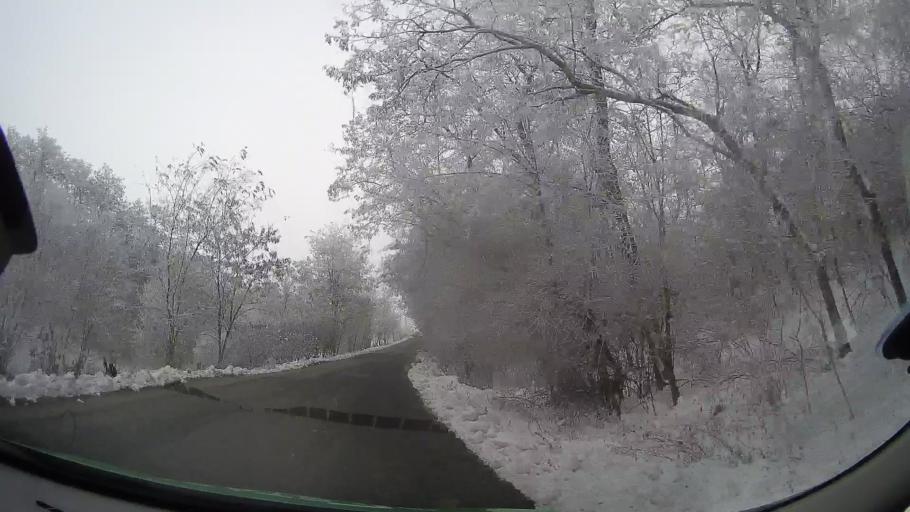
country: RO
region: Bacau
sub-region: Comuna Glavanesti
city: Frumuselu
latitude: 46.2643
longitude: 27.3257
